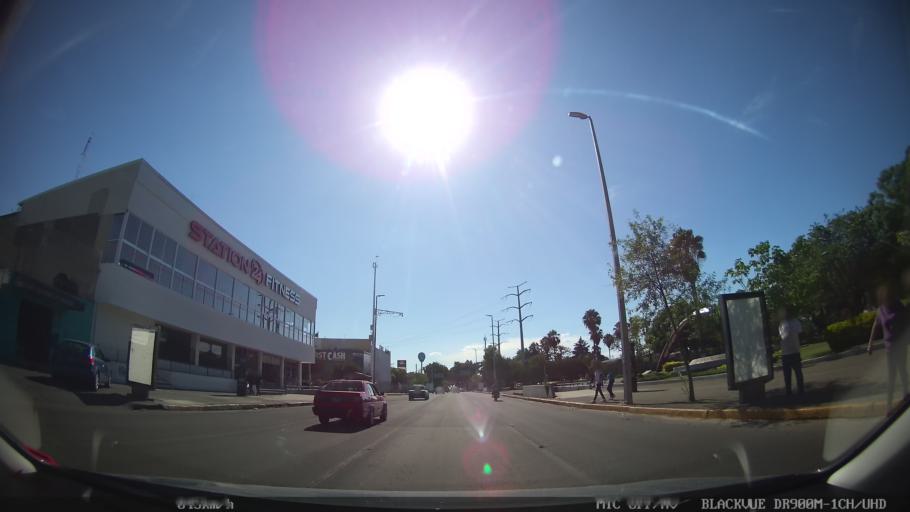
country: MX
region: Jalisco
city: Tlaquepaque
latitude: 20.6670
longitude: -103.3117
